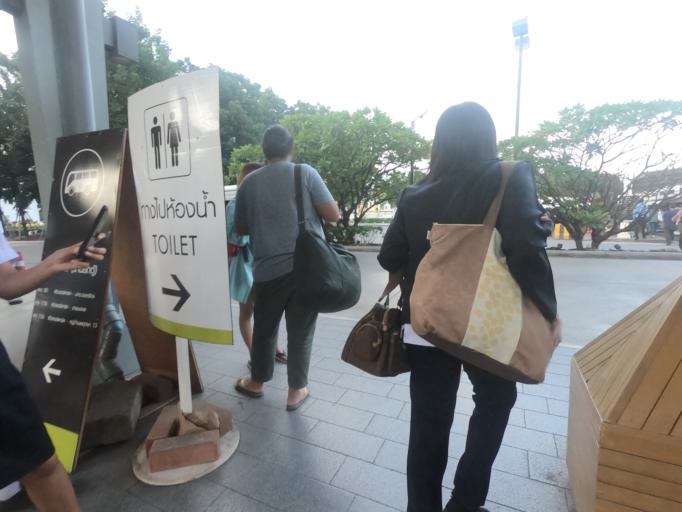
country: TH
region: Bangkok
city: Sai Mai
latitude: 13.9633
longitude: 100.6584
